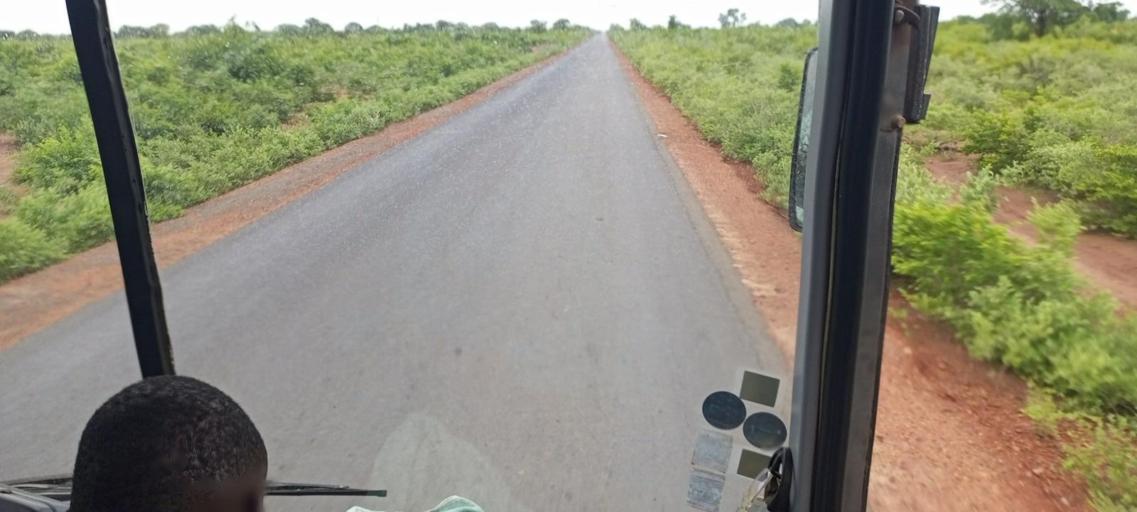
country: ML
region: Sikasso
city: Koutiala
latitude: 12.5645
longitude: -5.5965
